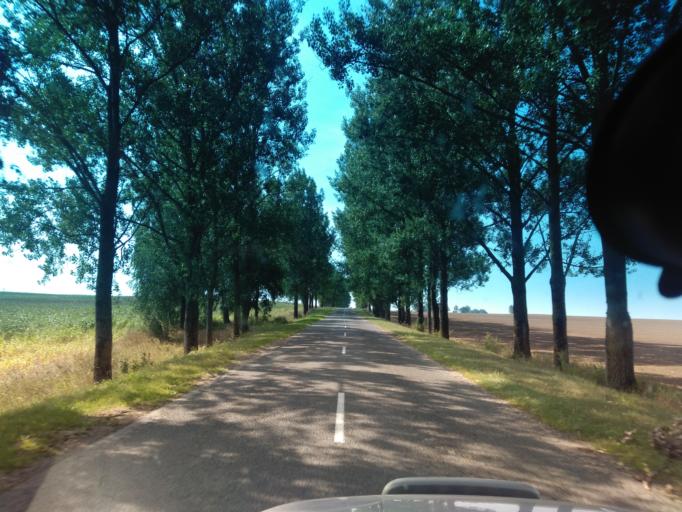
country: BY
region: Minsk
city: Kapyl'
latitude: 53.2660
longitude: 27.1973
